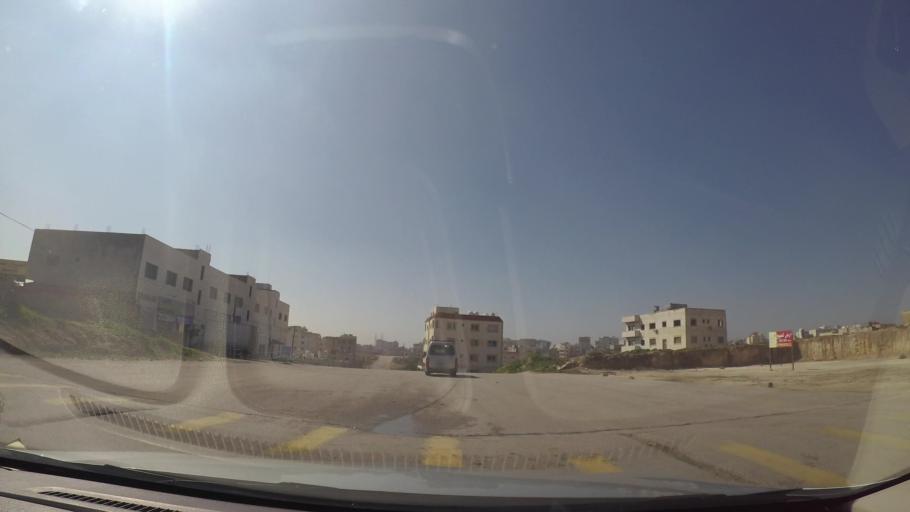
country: JO
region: Amman
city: Al Bunayyat ash Shamaliyah
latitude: 31.8963
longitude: 35.8980
